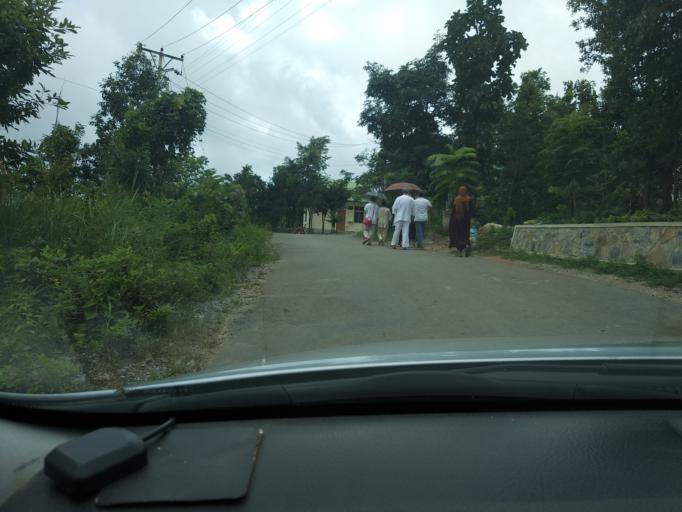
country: MM
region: Mandalay
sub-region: Pyin Oo Lwin District
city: Pyin Oo Lwin
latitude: 21.9124
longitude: 96.3834
